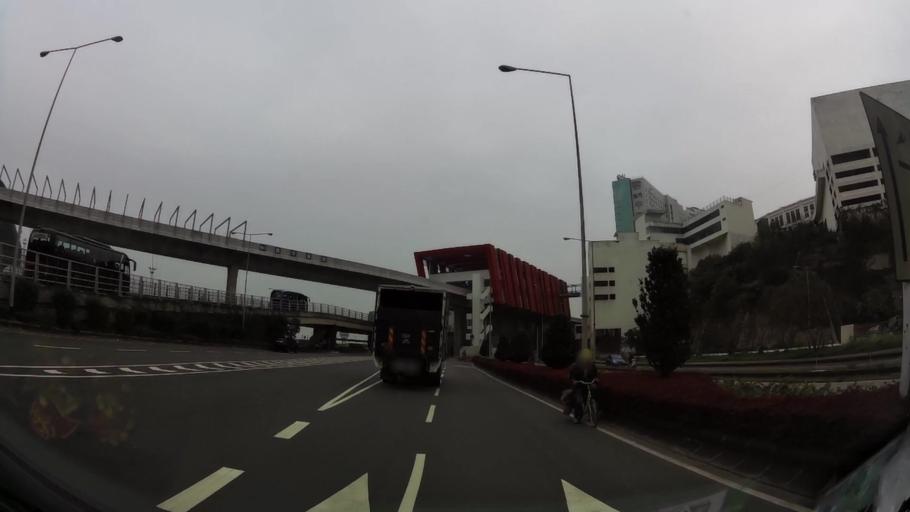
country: MO
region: Macau
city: Macau
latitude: 22.1606
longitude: 113.5743
